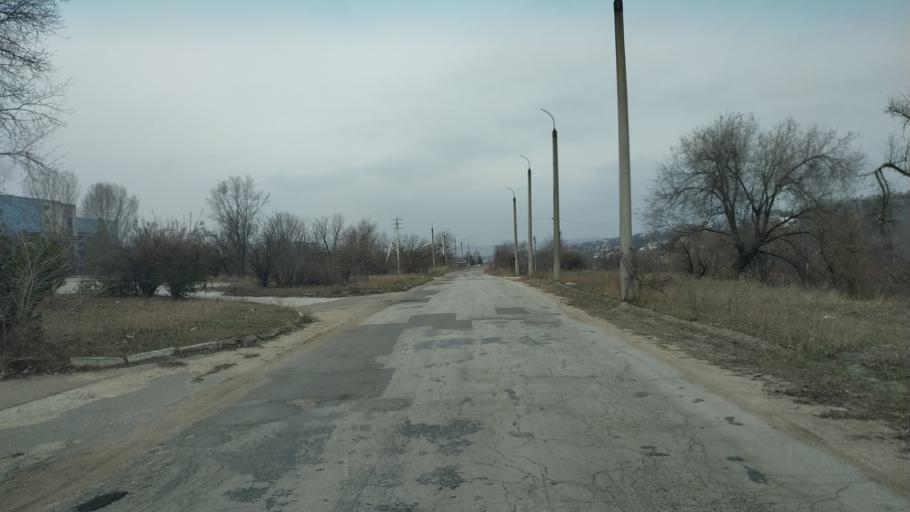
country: MD
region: Chisinau
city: Singera
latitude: 46.9048
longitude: 29.0186
